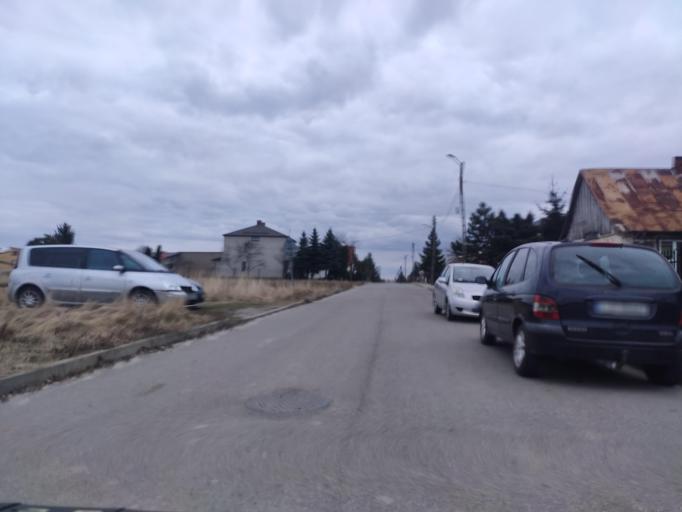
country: PL
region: Lublin Voivodeship
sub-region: Powiat lubartowski
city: Kock
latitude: 51.6390
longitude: 22.4340
